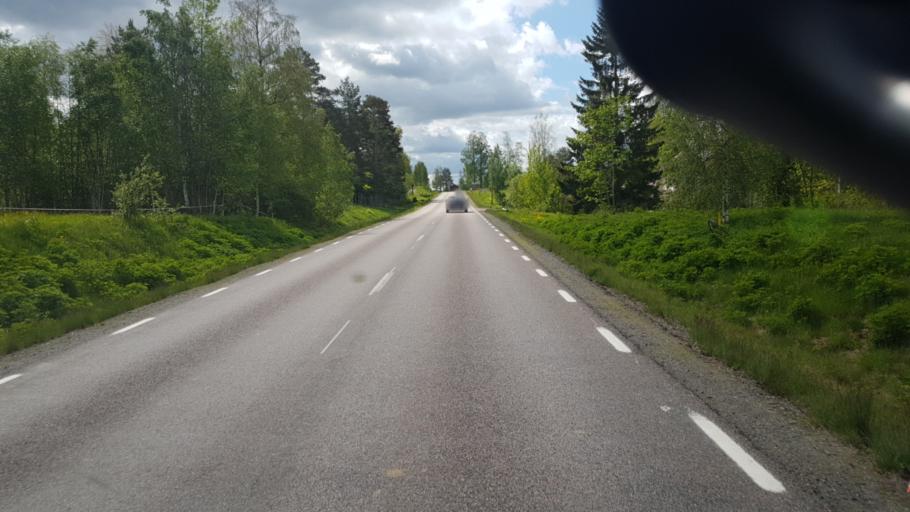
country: SE
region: Vaermland
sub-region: Eda Kommun
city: Amotfors
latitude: 59.6760
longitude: 12.1451
